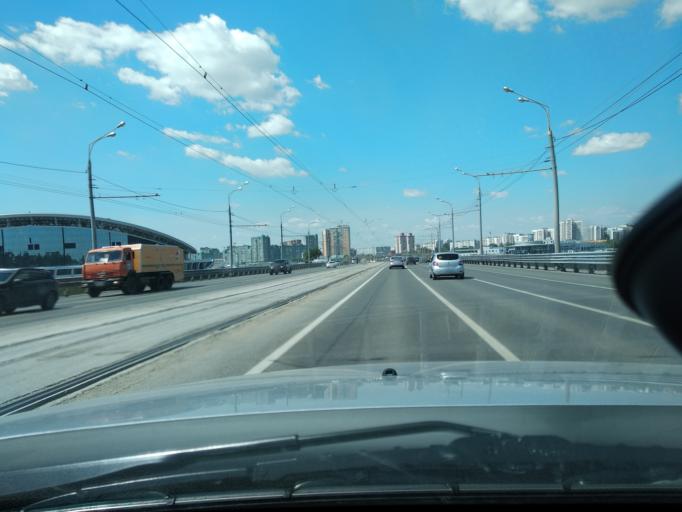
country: RU
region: Tatarstan
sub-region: Gorod Kazan'
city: Kazan
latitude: 55.8216
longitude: 49.1692
